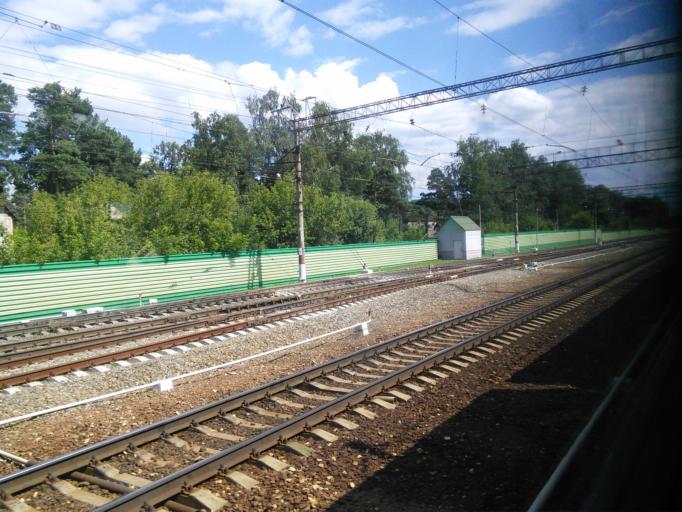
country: RU
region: Moskovskaya
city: Tomilino
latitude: 55.6591
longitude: 37.9429
